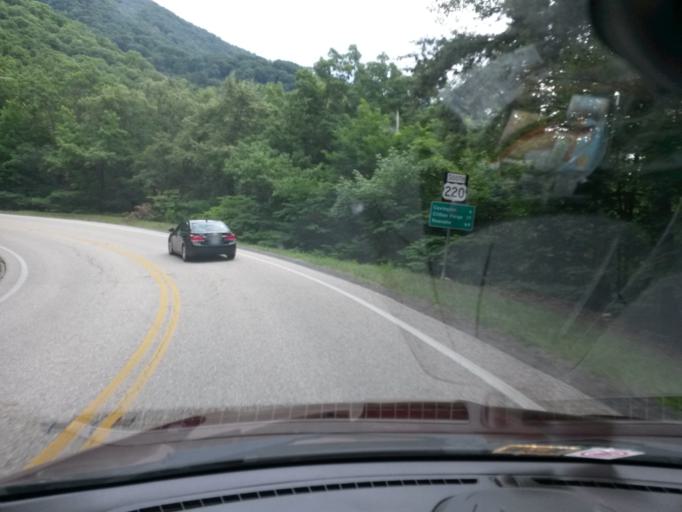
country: US
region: Virginia
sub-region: City of Covington
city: Covington
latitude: 37.8534
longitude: -79.9646
